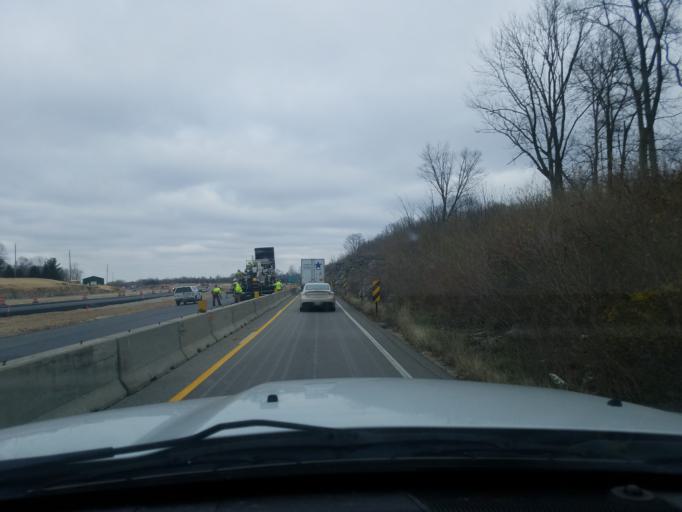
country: US
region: Indiana
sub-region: Monroe County
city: Bloomington
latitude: 39.2587
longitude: -86.5244
